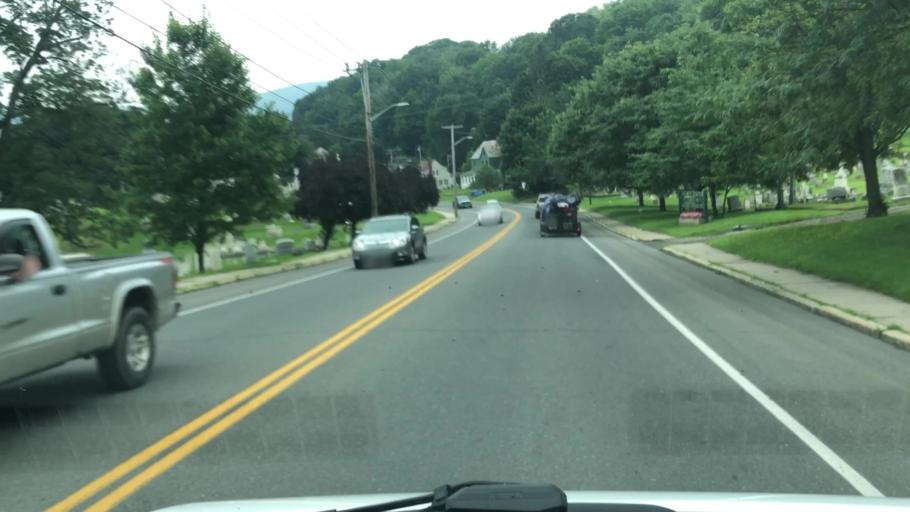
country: US
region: Massachusetts
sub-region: Berkshire County
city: North Adams
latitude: 42.7010
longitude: -73.1227
